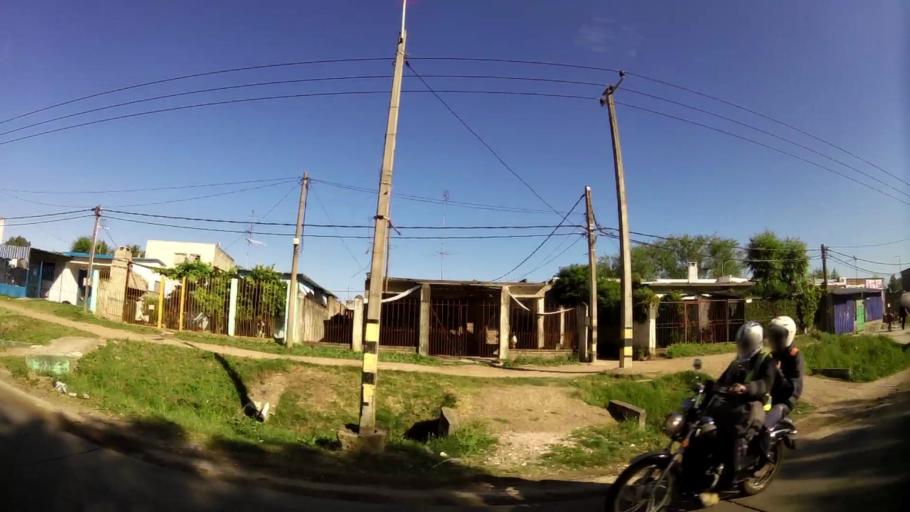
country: UY
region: Canelones
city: La Paz
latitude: -34.8258
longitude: -56.1817
